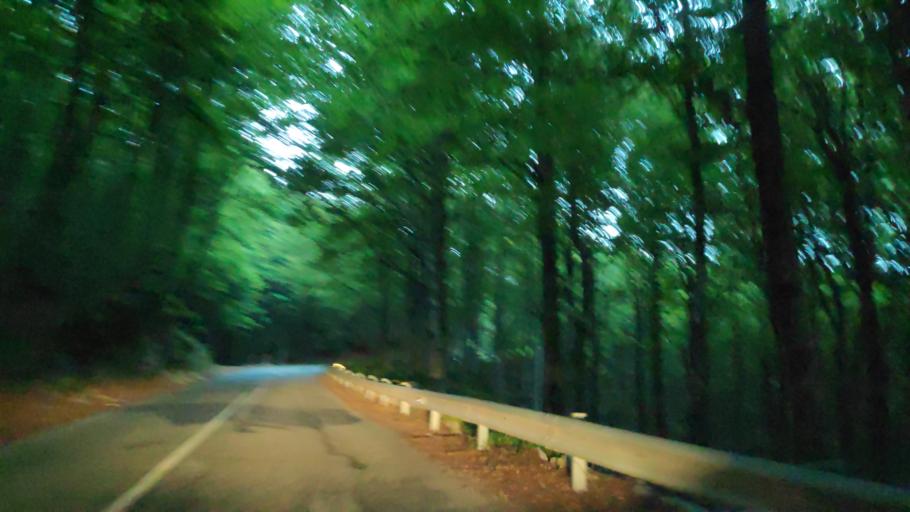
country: IT
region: Calabria
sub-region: Provincia di Vibo-Valentia
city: Mongiana
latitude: 38.5175
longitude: 16.3415
